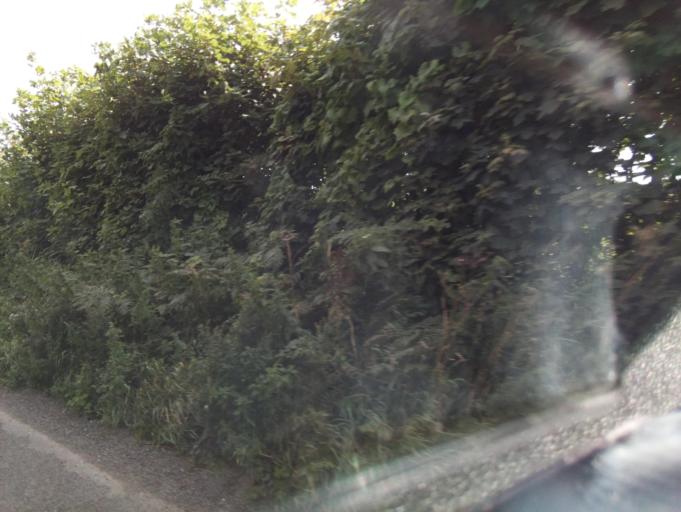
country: GB
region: England
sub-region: Devon
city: Totnes
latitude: 50.4255
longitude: -3.7475
